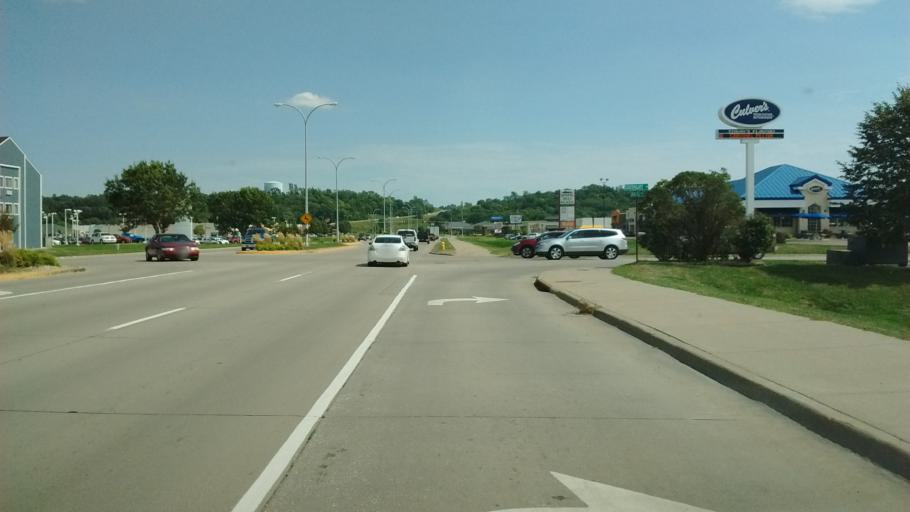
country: US
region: Iowa
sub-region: Woodbury County
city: Sergeant Bluff
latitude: 42.4353
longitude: -96.3687
